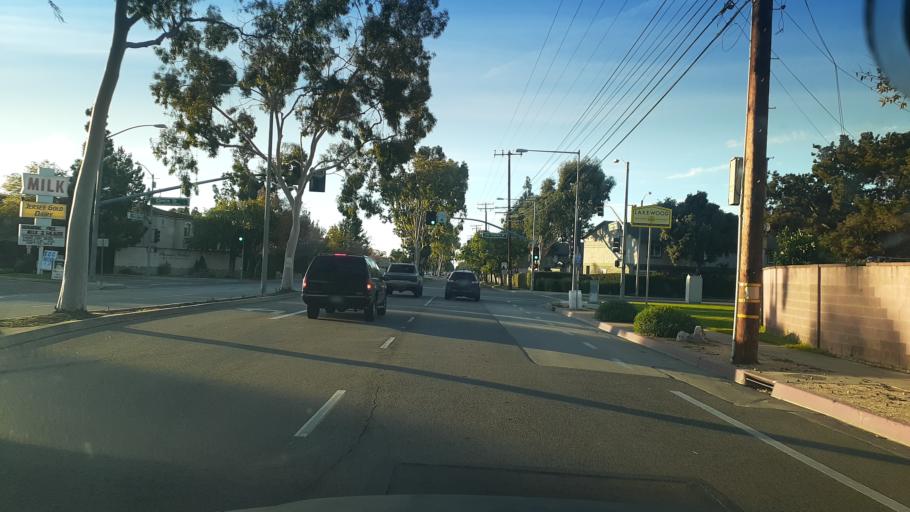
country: US
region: California
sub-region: Los Angeles County
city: Artesia
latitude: 33.8493
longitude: -118.0818
